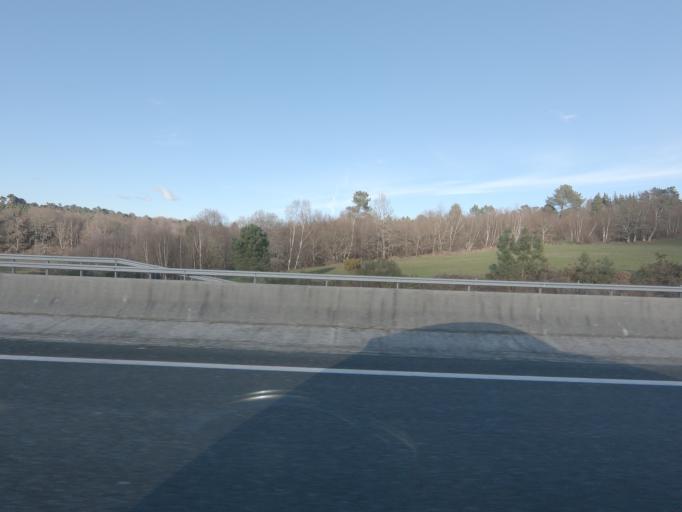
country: ES
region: Galicia
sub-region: Provincia de Pontevedra
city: Lalin
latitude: 42.6339
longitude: -8.1284
